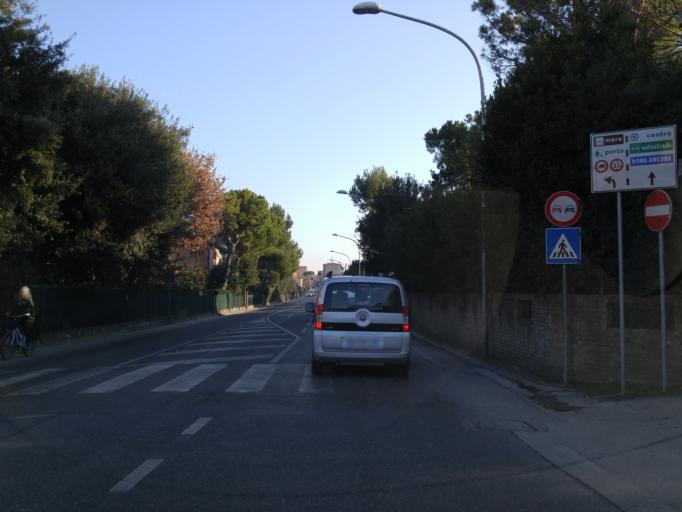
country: IT
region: The Marches
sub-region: Provincia di Pesaro e Urbino
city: Fano
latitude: 43.8498
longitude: 13.0078
